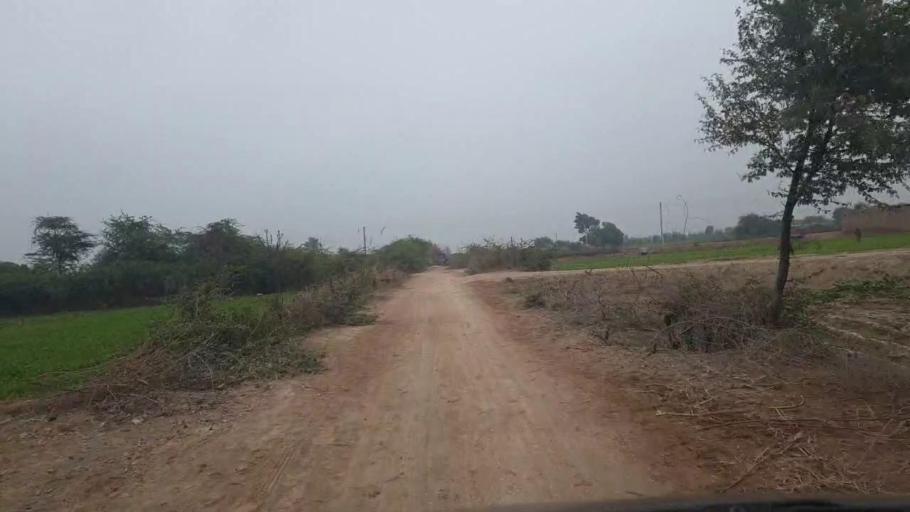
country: PK
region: Sindh
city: Tando Adam
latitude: 25.8407
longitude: 68.7132
